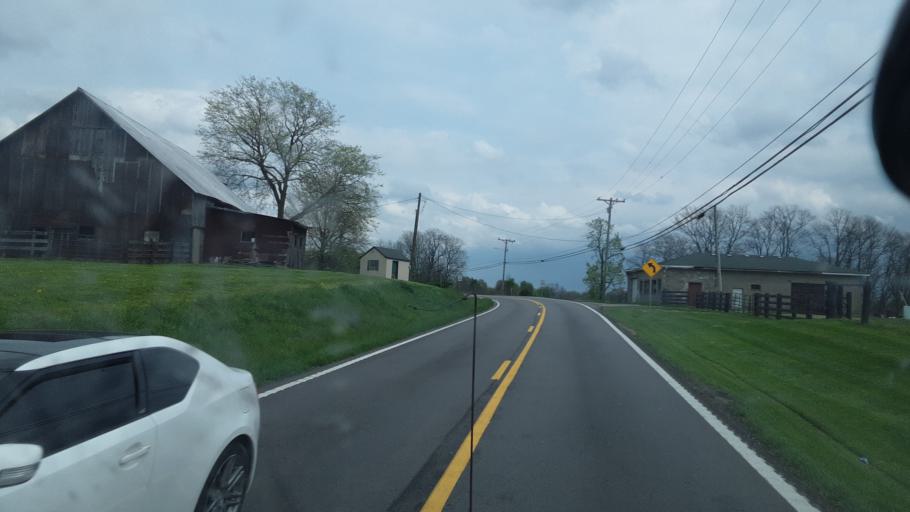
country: US
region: Kentucky
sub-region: Grant County
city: Dry Ridge
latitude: 38.6790
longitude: -84.6164
